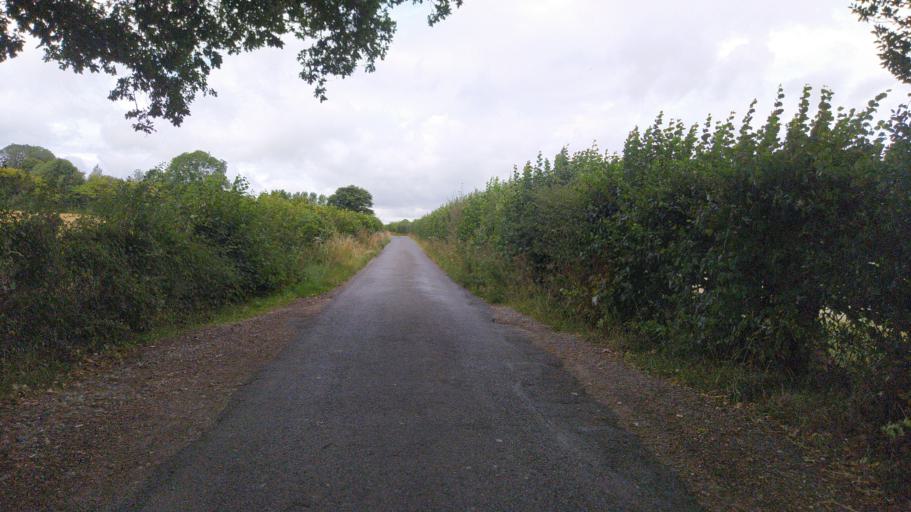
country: GB
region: England
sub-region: Hampshire
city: Petersfield
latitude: 50.9892
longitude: -0.9761
